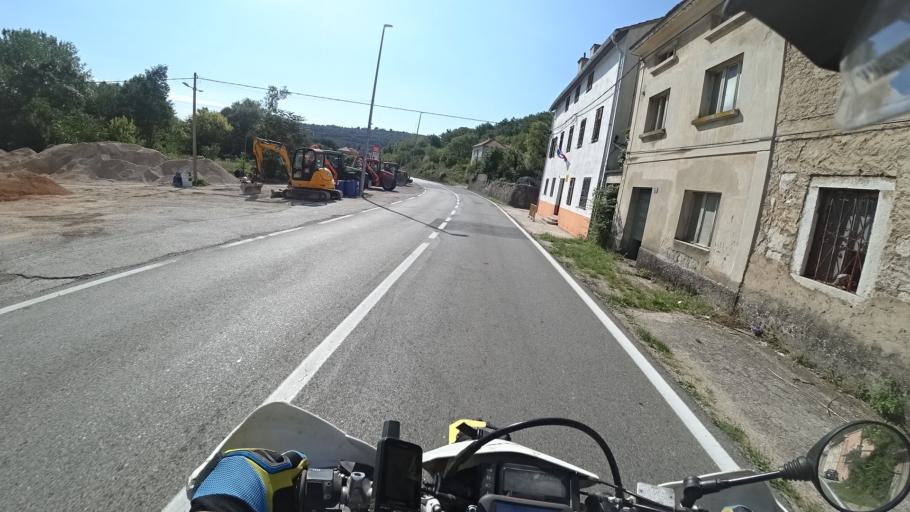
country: HR
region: Sibensko-Kniniska
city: Knin
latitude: 44.0310
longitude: 16.1901
